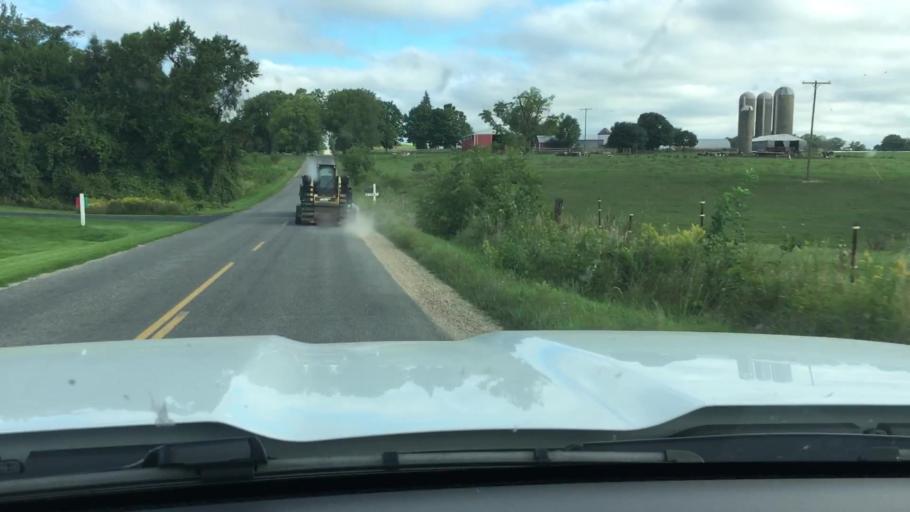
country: US
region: Michigan
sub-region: Kent County
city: Byron Center
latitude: 42.8066
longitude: -85.8026
